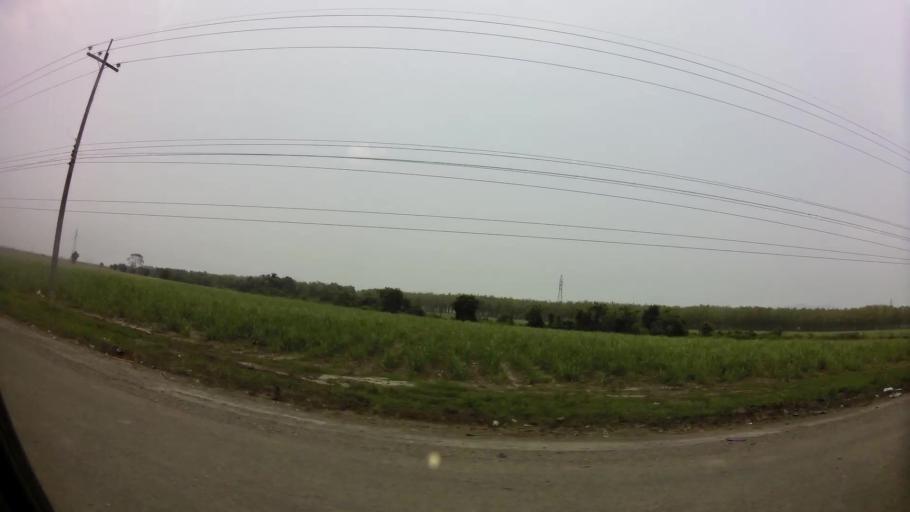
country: HN
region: Cortes
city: La Lima
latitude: 15.4116
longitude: -87.8721
